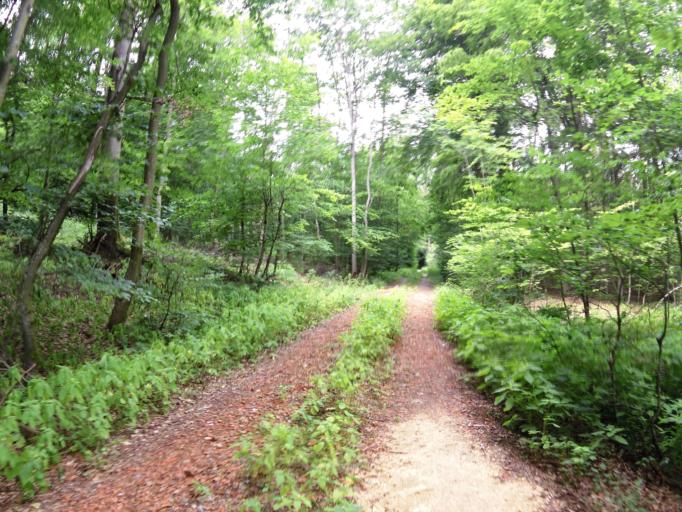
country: DE
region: Bavaria
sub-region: Regierungsbezirk Unterfranken
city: Geroldshausen
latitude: 49.7139
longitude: 9.8834
